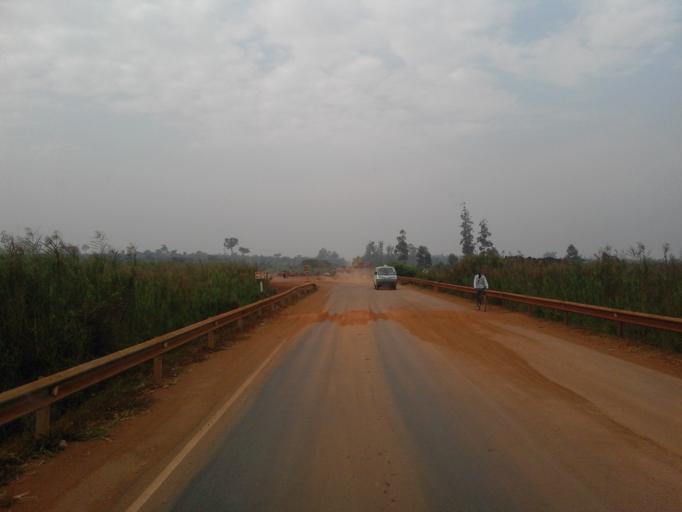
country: UG
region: Eastern Region
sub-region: Busia District
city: Busia
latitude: 0.5867
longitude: 34.0537
